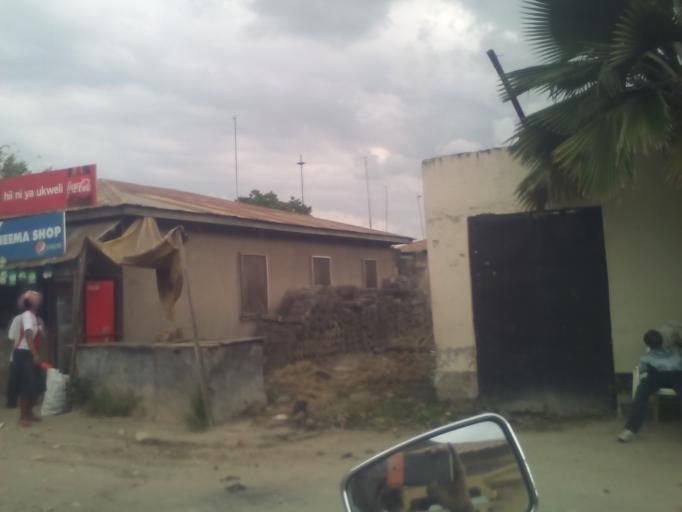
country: TZ
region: Dar es Salaam
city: Dar es Salaam
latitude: -6.8410
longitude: 39.2747
